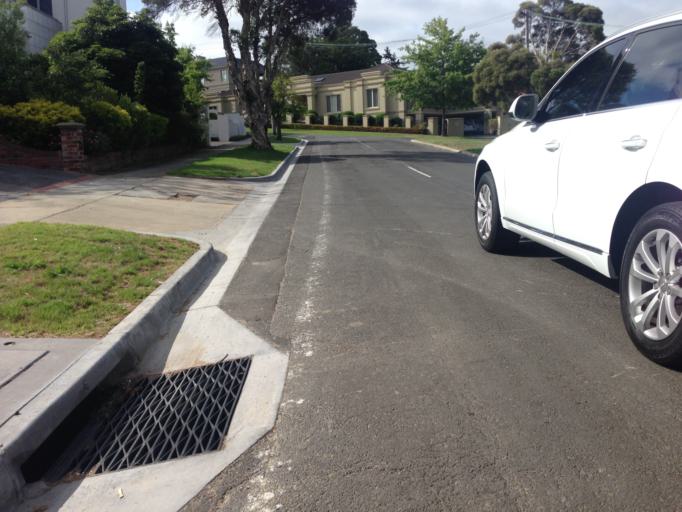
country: AU
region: Victoria
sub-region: Boroondara
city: Balwyn North
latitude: -37.7964
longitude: 145.0859
